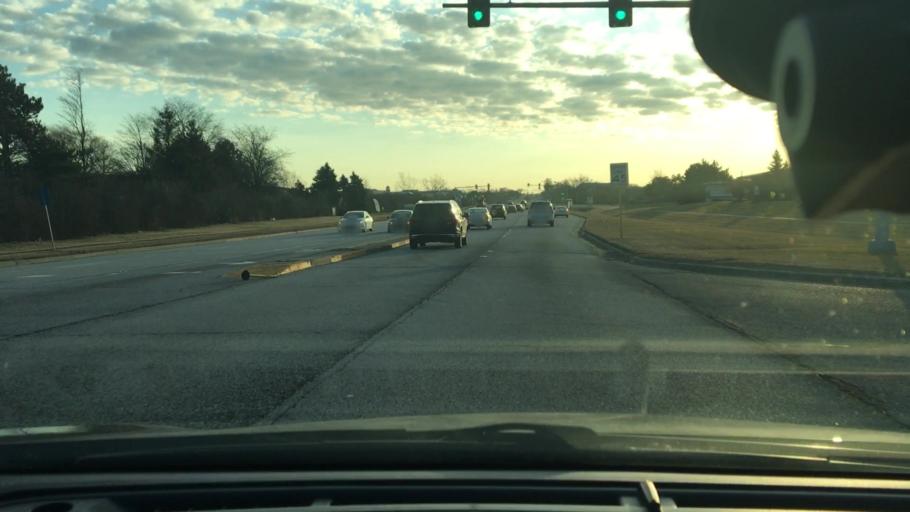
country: US
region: Illinois
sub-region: Cook County
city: Northbrook
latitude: 42.1054
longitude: -87.8147
